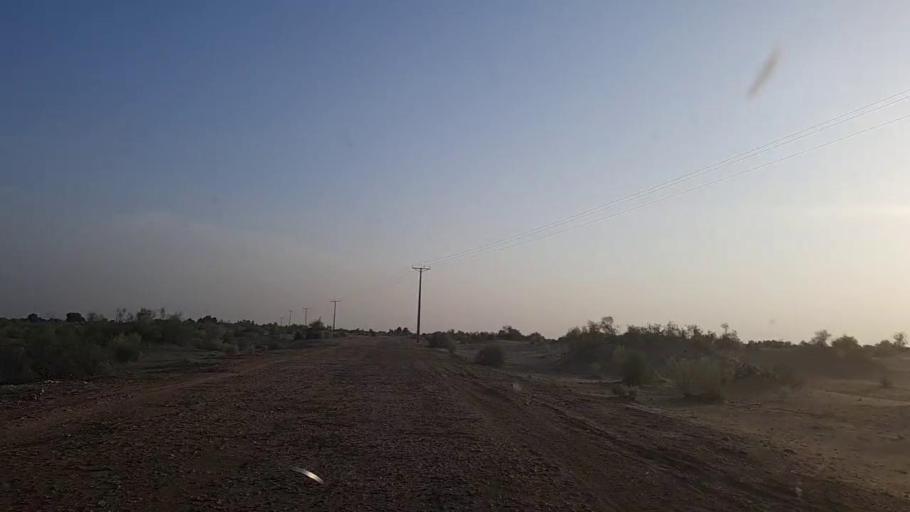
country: PK
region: Sindh
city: Khanpur
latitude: 27.6424
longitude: 69.4562
